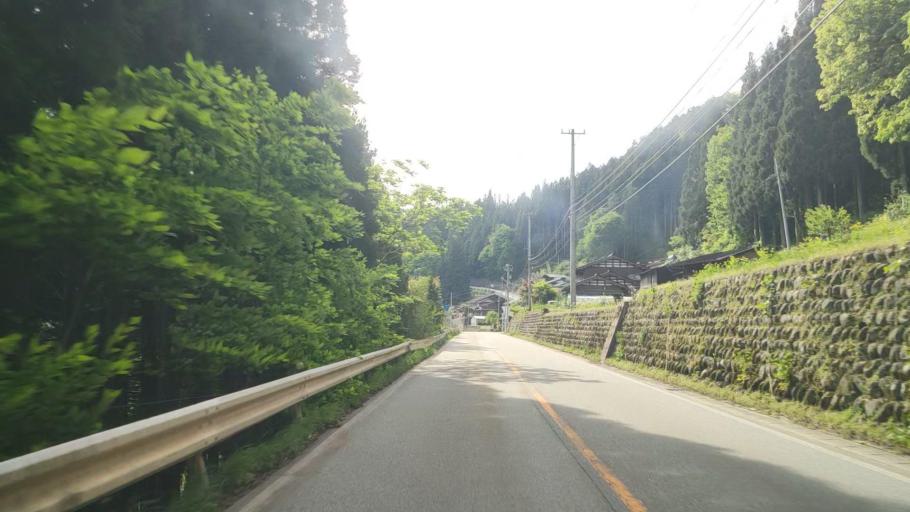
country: JP
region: Gifu
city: Takayama
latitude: 36.3015
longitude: 137.3425
